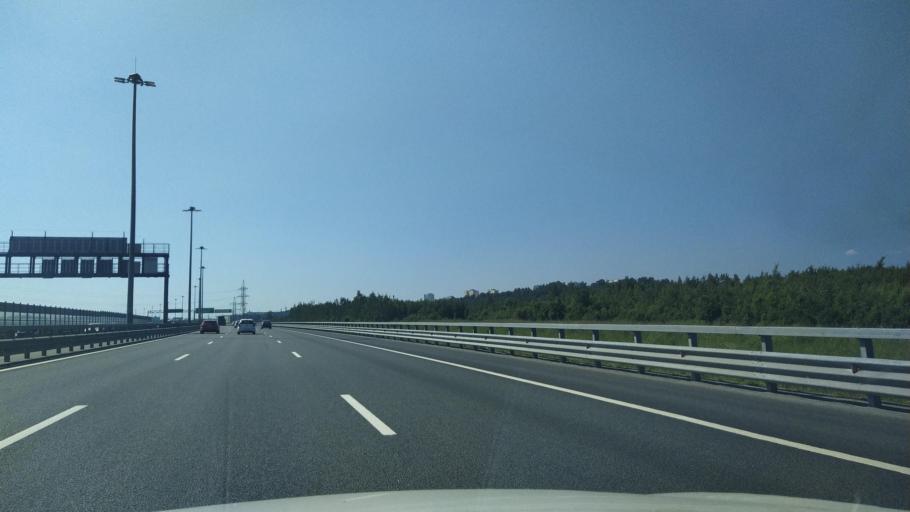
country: RU
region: St.-Petersburg
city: Pargolovo
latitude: 60.0982
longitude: 30.2932
